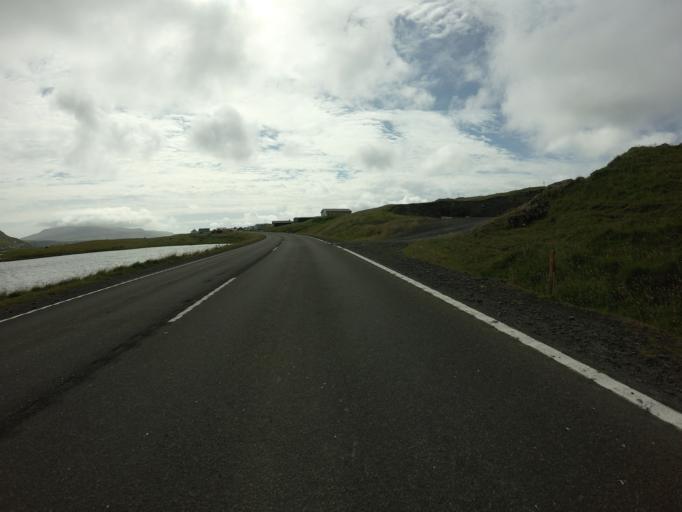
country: FO
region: Sandoy
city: Sandur
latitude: 61.8444
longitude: -6.8265
